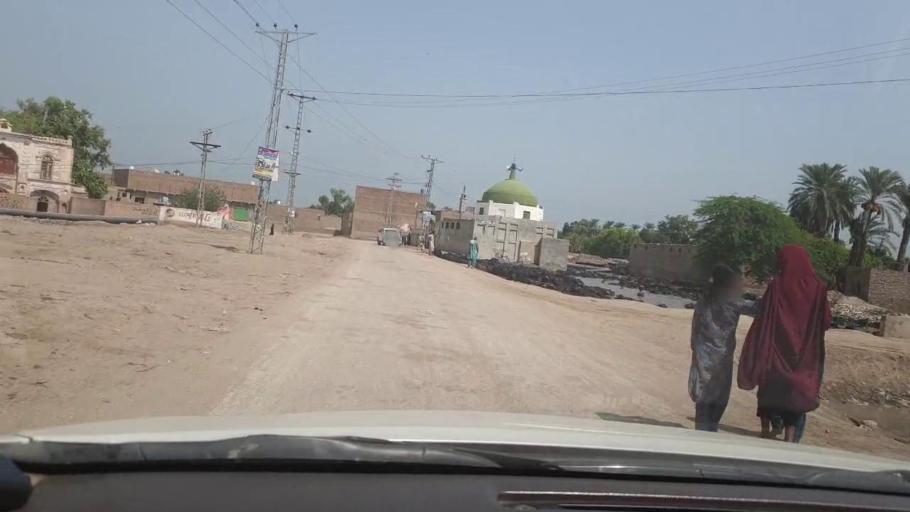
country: PK
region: Sindh
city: Shikarpur
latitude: 27.9427
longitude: 68.6372
